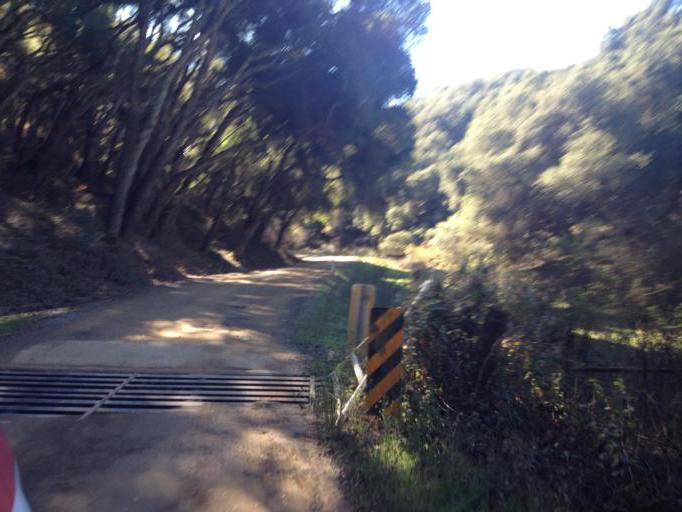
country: US
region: California
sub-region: San Luis Obispo County
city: Avila Beach
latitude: 35.2446
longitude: -120.7767
